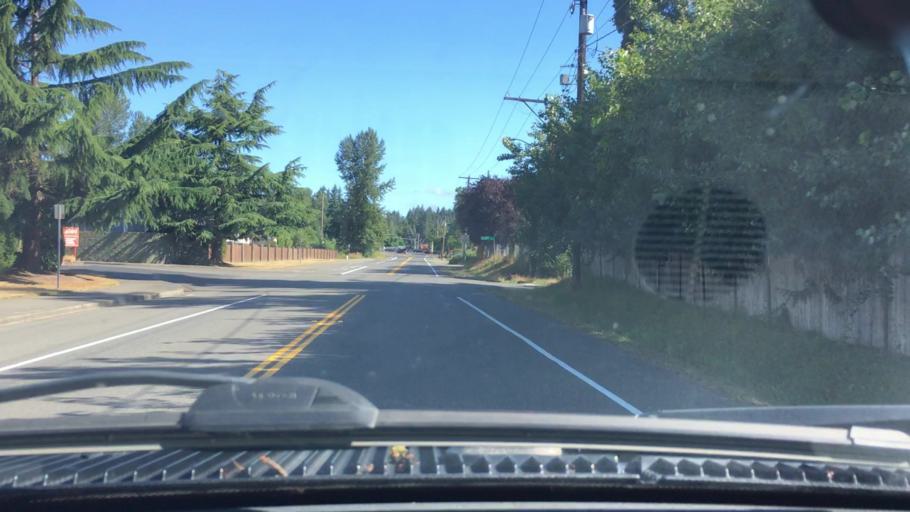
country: US
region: Washington
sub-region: King County
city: Covington
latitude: 47.3550
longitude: -122.1389
